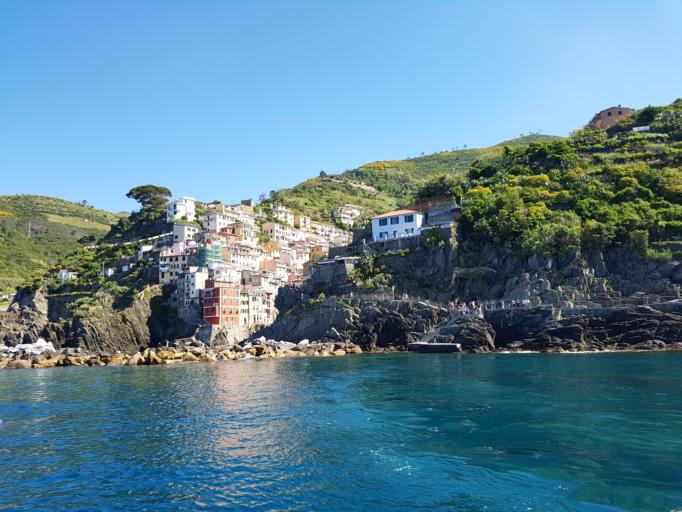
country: IT
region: Liguria
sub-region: Provincia di La Spezia
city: Riomaggiore
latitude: 44.0969
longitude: 9.7372
